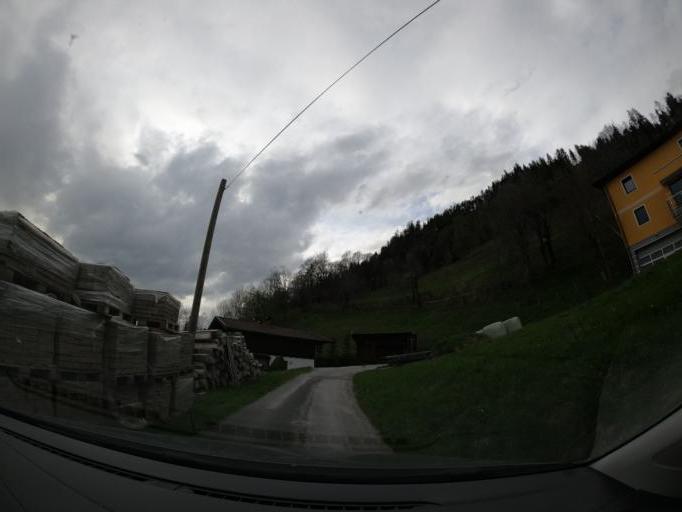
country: AT
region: Salzburg
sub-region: Politischer Bezirk Zell am See
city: Lend
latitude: 47.3048
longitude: 13.0498
